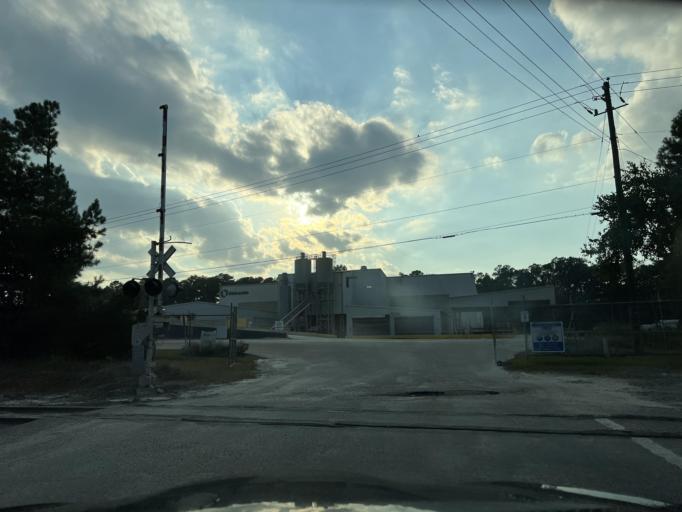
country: US
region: North Carolina
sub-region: Wake County
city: Raleigh
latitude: 35.7305
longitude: -78.6636
